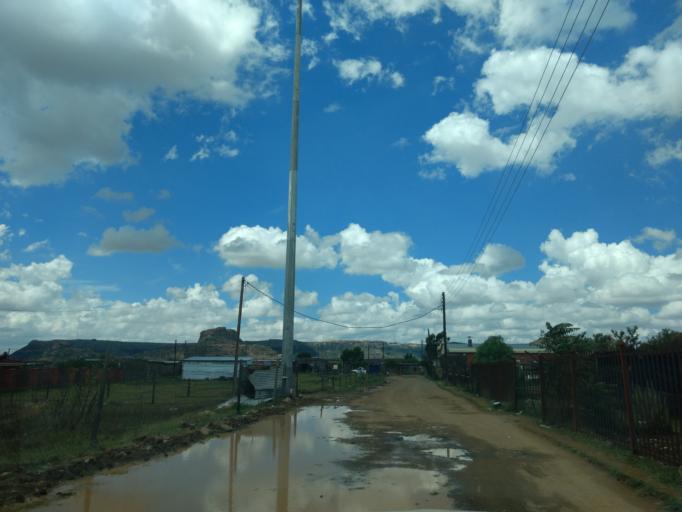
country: LS
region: Maseru
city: Maseru
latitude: -29.3678
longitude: 27.5137
